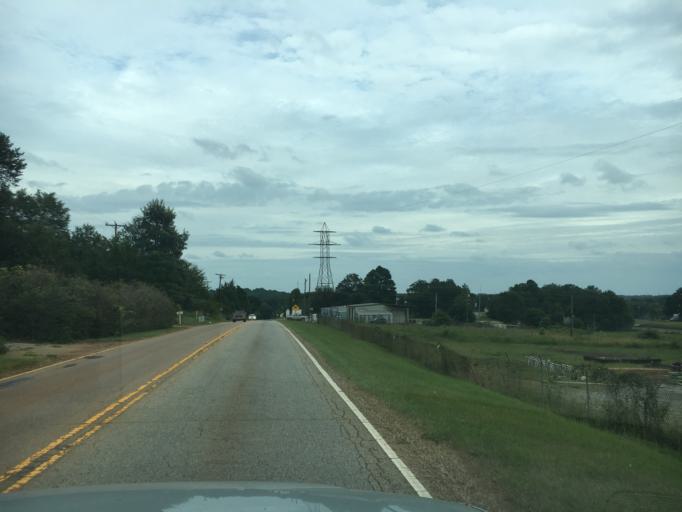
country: US
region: South Carolina
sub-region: Spartanburg County
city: Duncan
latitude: 34.9369
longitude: -82.1702
